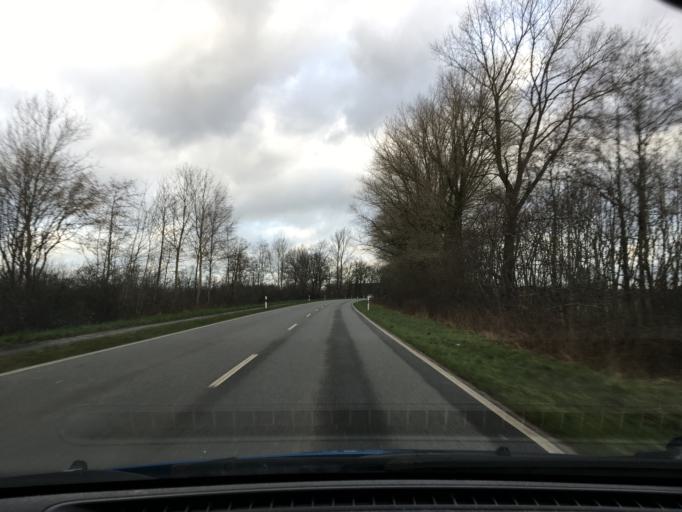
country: DE
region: Schleswig-Holstein
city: Kaisborstel
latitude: 54.0103
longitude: 9.4828
